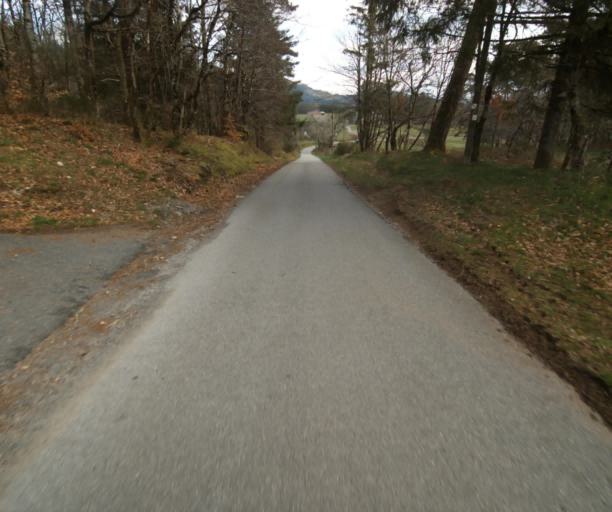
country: FR
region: Limousin
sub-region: Departement de la Correze
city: Correze
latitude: 45.3884
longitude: 1.8802
